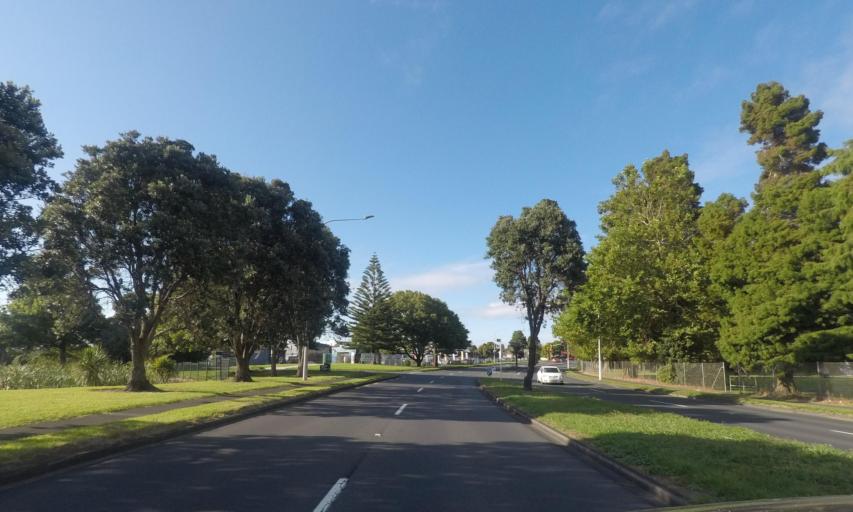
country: NZ
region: Auckland
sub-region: Auckland
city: Rosebank
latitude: -36.9008
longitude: 174.6829
